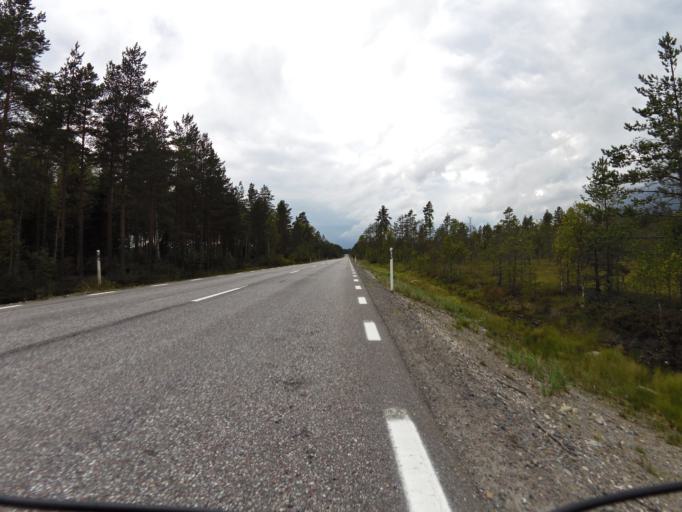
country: SE
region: Gaevleborg
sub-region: Gavle Kommun
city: Norrsundet
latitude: 60.8978
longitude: 16.9438
